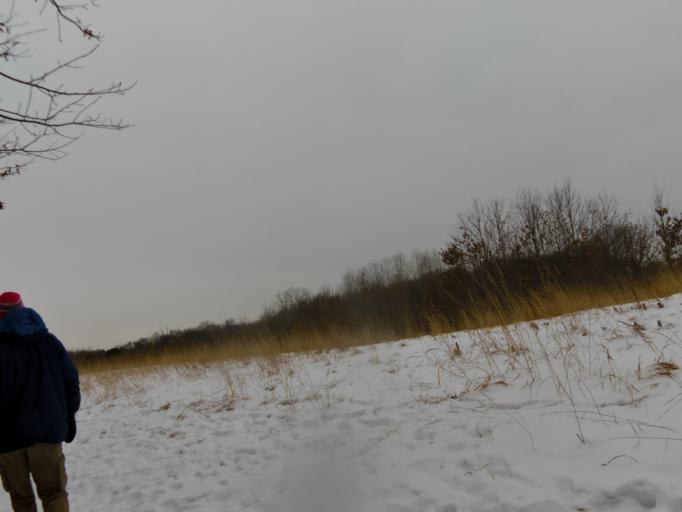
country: US
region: Minnesota
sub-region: Dakota County
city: Inver Grove Heights
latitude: 44.8606
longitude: -93.0745
